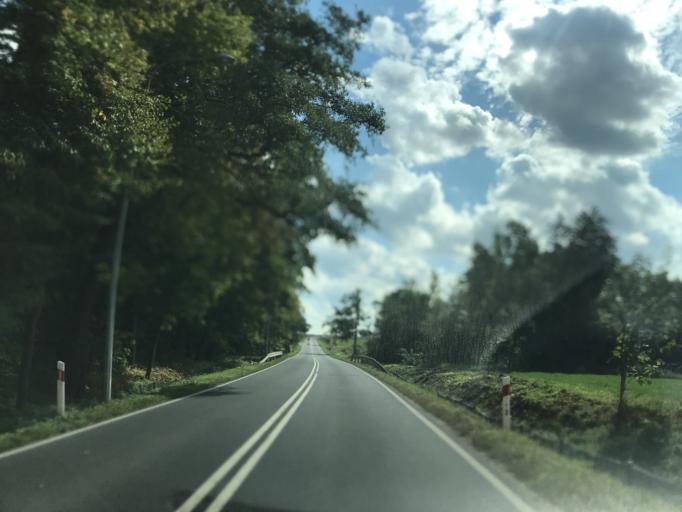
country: PL
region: Warmian-Masurian Voivodeship
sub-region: Powiat ilawski
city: Lubawa
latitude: 53.4237
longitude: 19.7790
